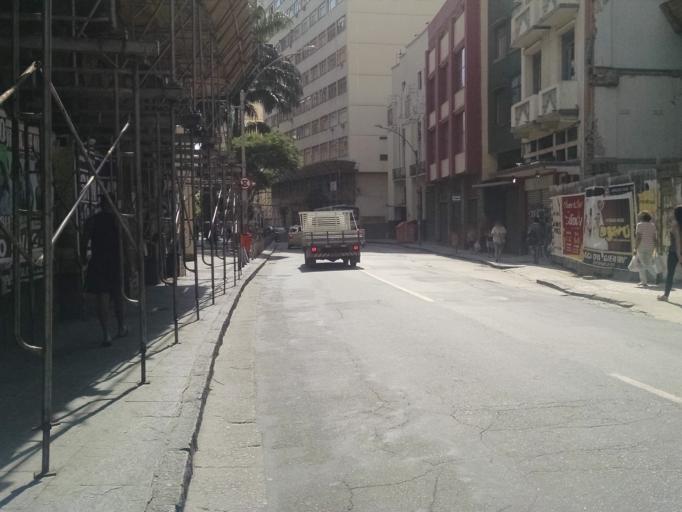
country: BR
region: Rio de Janeiro
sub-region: Rio De Janeiro
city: Rio de Janeiro
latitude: -22.9144
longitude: -43.1840
